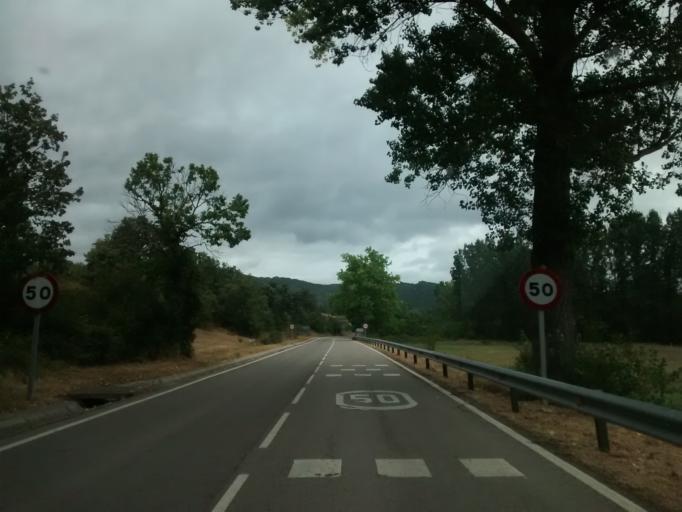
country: ES
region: Castille and Leon
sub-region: Provincia de Palencia
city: Berzosilla
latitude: 42.7917
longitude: -3.9869
